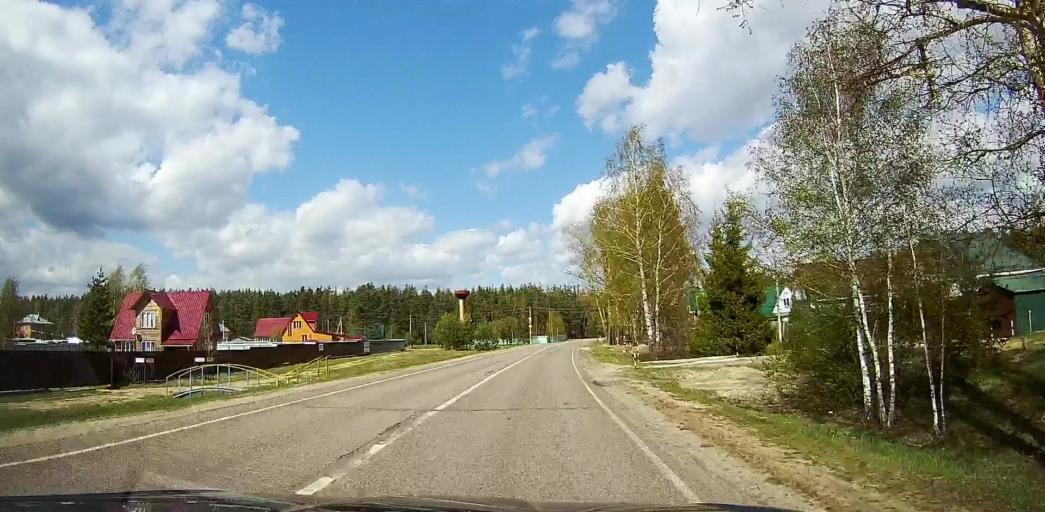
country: RU
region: Moskovskaya
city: Davydovo
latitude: 55.5610
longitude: 38.8130
